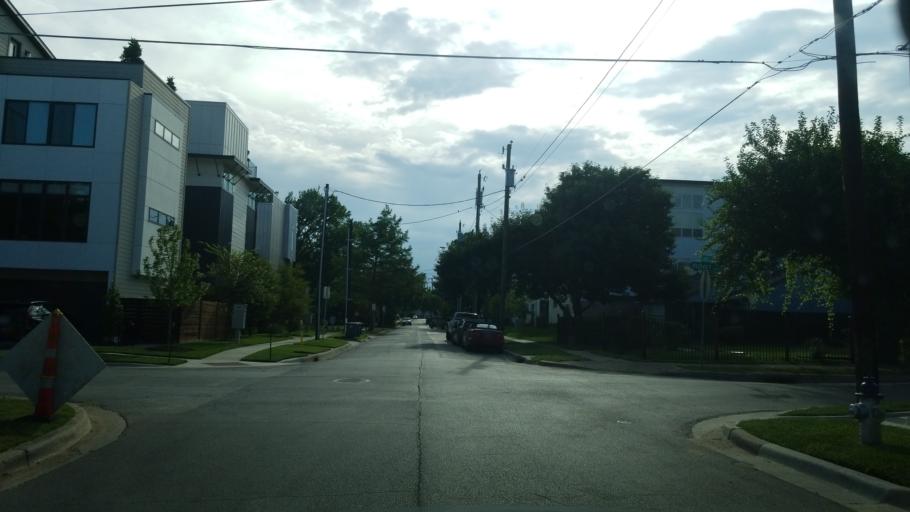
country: US
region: Texas
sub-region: Dallas County
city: Highland Park
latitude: 32.8089
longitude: -96.7668
